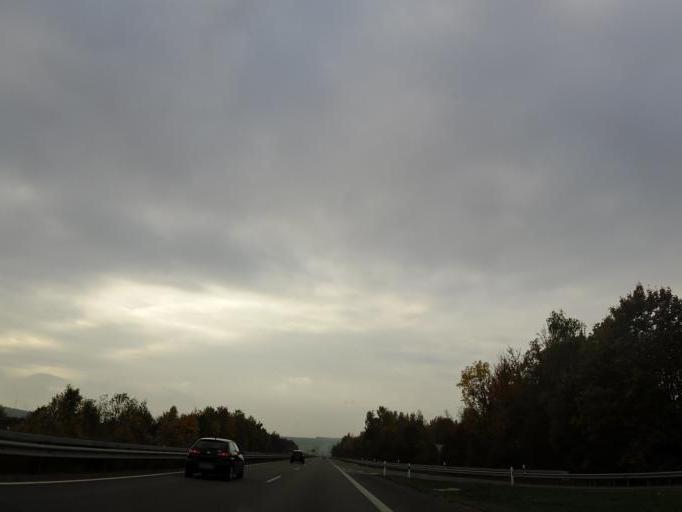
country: DE
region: Rheinland-Pfalz
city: Alzey
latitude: 49.7469
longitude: 8.0848
